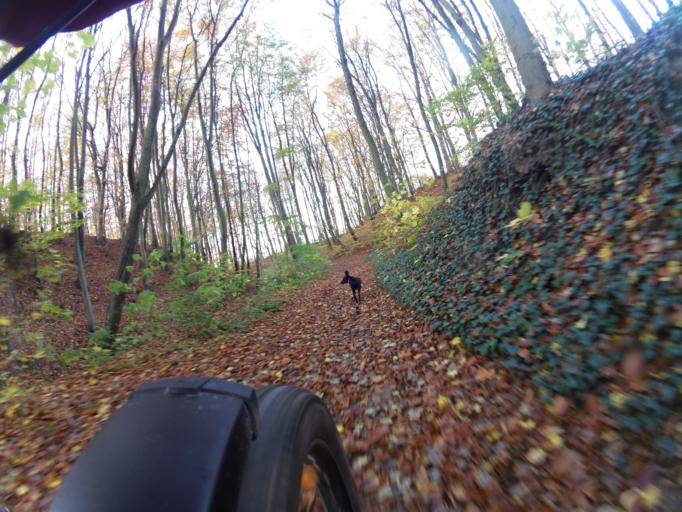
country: PL
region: Pomeranian Voivodeship
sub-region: Powiat pucki
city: Krokowa
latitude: 54.7712
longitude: 18.1736
